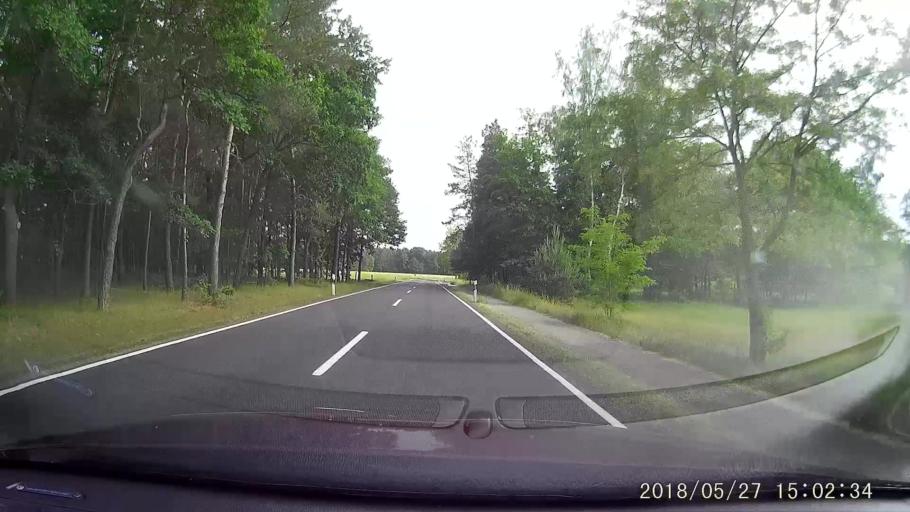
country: DE
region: Saxony
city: Mucka
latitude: 51.3271
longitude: 14.7016
